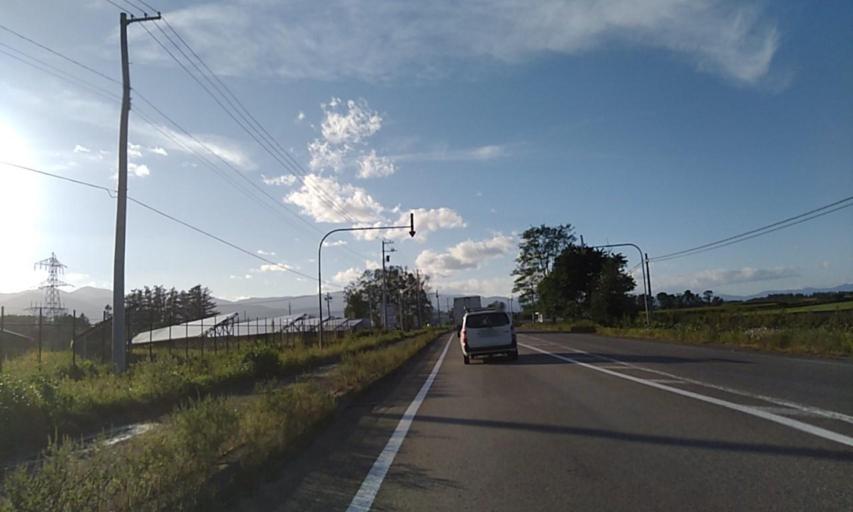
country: JP
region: Hokkaido
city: Otofuke
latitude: 42.9419
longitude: 142.9518
